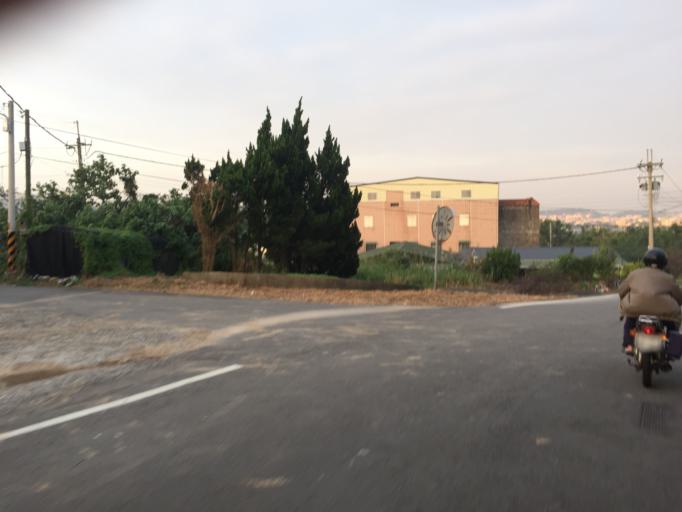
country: TW
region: Taiwan
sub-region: Miaoli
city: Miaoli
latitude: 24.4736
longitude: 120.7764
